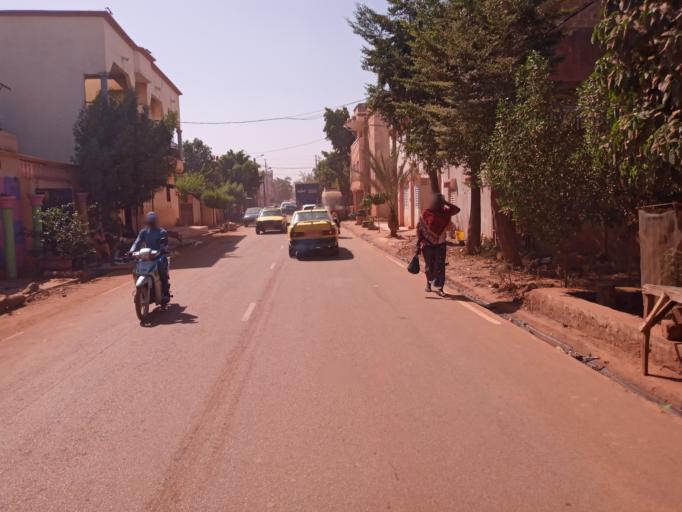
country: ML
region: Bamako
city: Bamako
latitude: 12.6128
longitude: -7.9561
